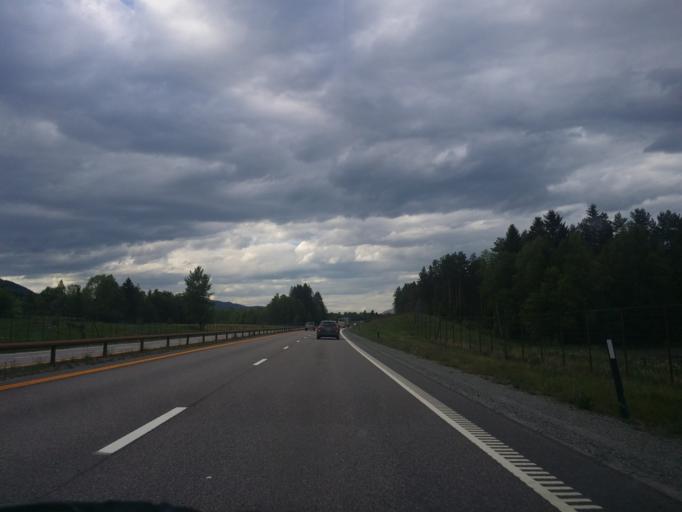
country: NO
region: Akershus
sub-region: Eidsvoll
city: Eidsvoll
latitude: 60.3637
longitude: 11.2044
